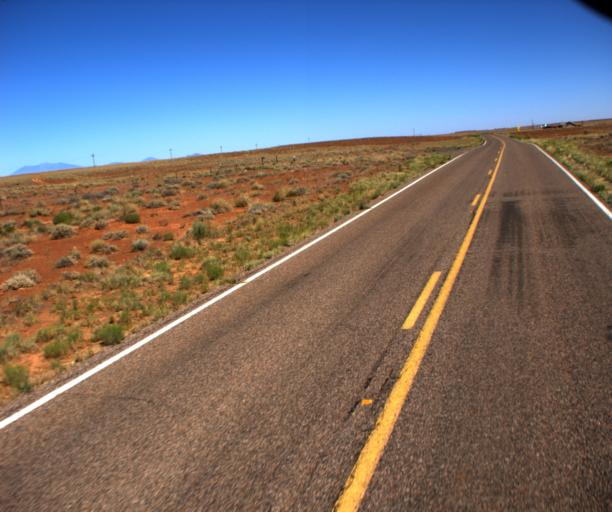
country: US
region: Arizona
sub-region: Coconino County
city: LeChee
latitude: 35.1704
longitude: -110.9171
